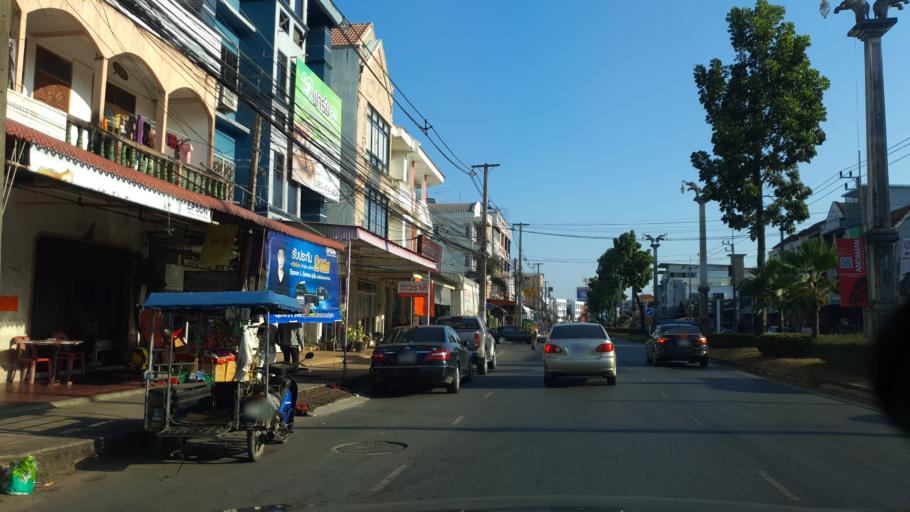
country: TH
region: Krabi
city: Krabi
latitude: 8.0696
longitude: 98.9133
